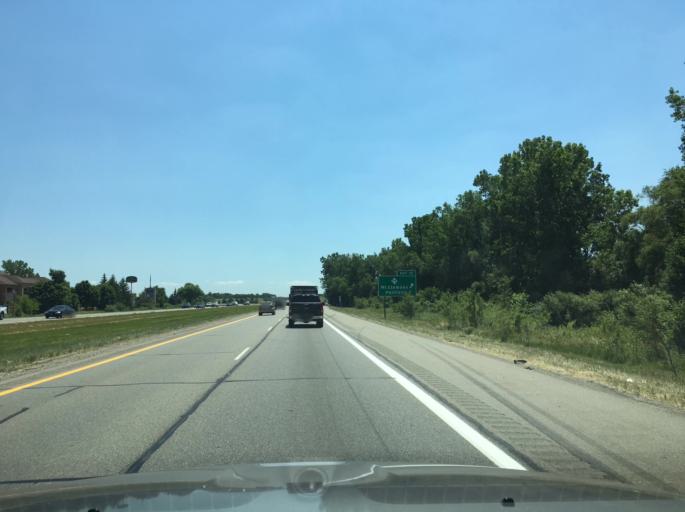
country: US
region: Michigan
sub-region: Macomb County
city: Utica
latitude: 42.6338
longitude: -83.0135
